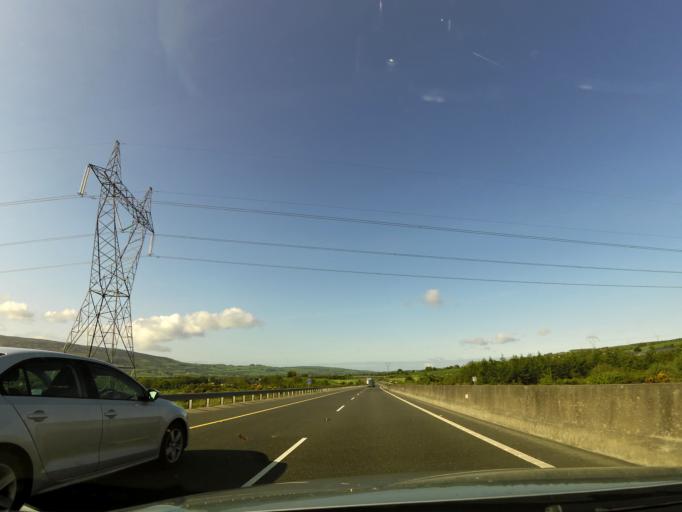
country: IE
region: Munster
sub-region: North Tipperary
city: Nenagh
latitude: 52.8299
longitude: -8.2939
